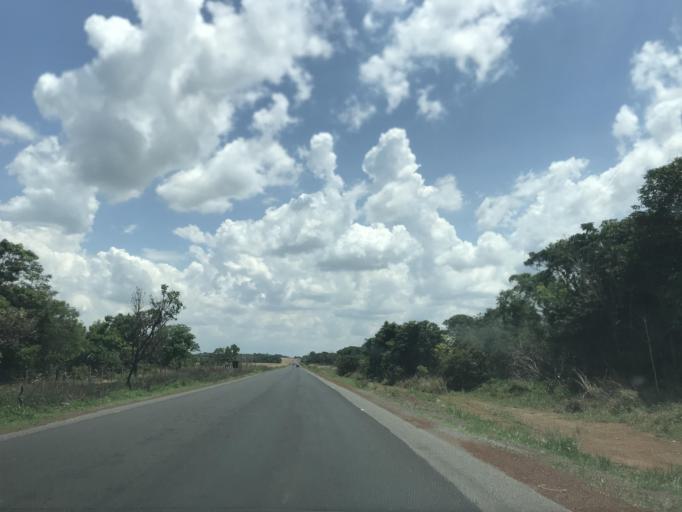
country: BR
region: Goias
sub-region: Piracanjuba
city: Piracanjuba
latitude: -17.3048
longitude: -48.7994
